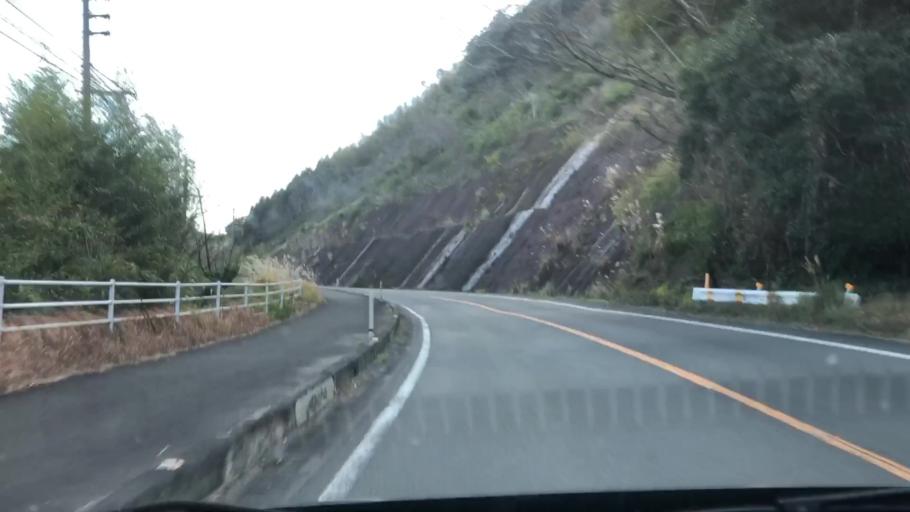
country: JP
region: Kagoshima
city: Satsumasendai
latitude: 31.8574
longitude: 130.3161
